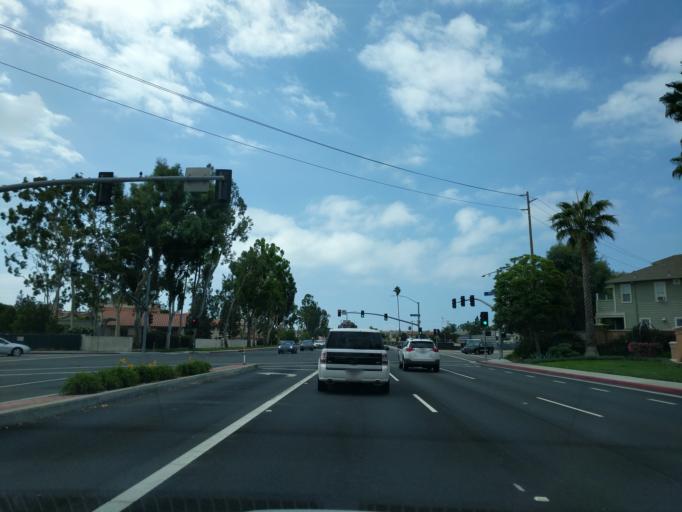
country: US
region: California
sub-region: Orange County
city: Huntington Beach
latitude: 33.6870
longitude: -117.9974
